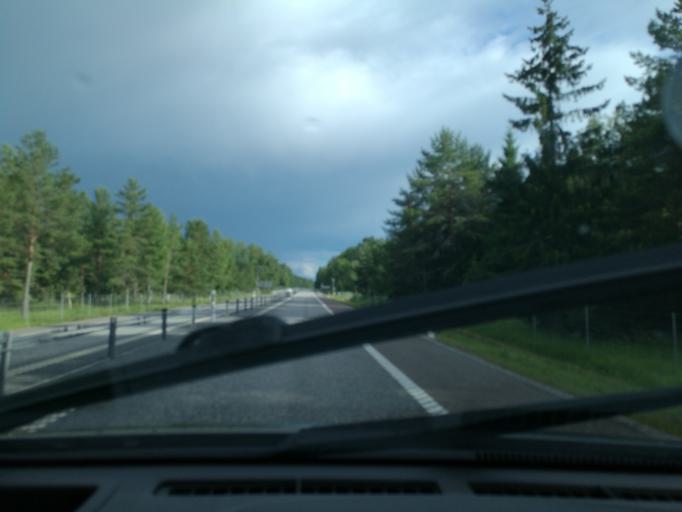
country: SE
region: Vaestmanland
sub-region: Surahammars Kommun
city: Surahammar
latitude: 59.7209
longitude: 16.2374
